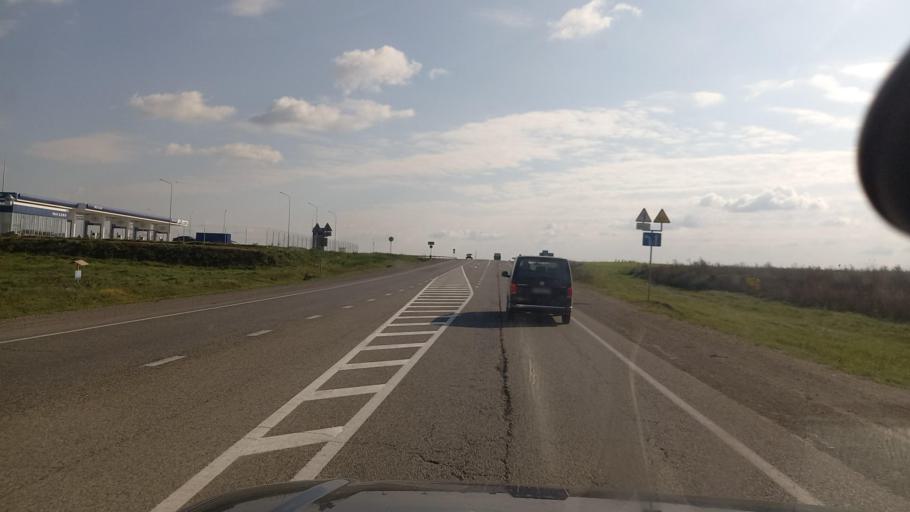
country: RU
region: Krasnodarskiy
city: Abinsk
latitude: 44.8742
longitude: 38.1130
